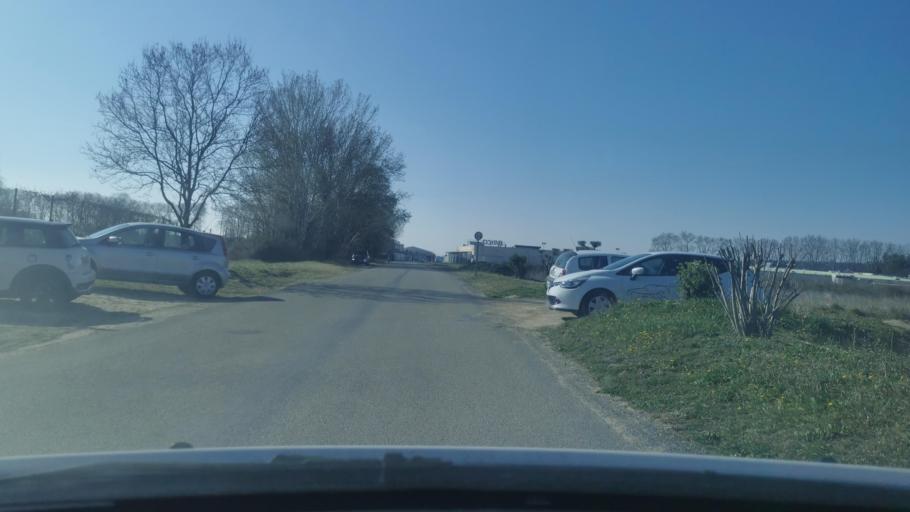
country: FR
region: Languedoc-Roussillon
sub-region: Departement du Gard
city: Montaren-et-Saint-Mediers
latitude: 44.0280
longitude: 4.3906
